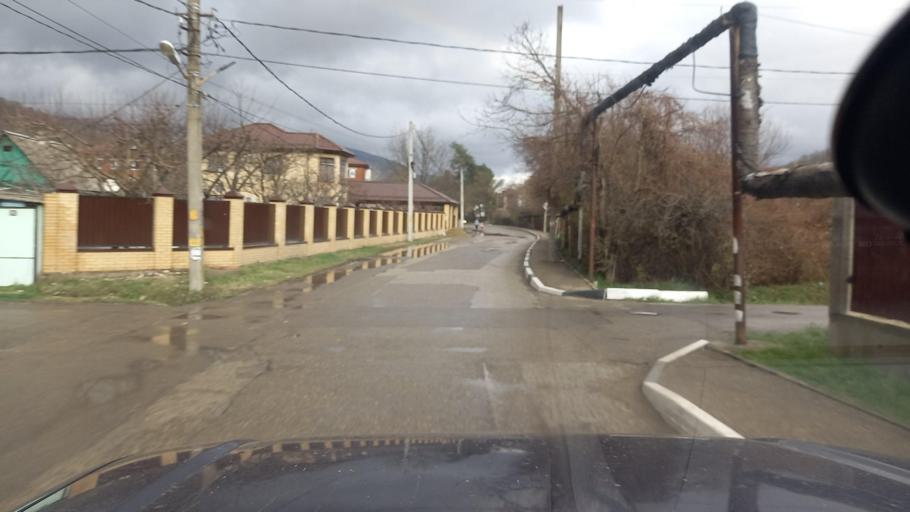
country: RU
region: Krasnodarskiy
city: Pshada
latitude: 44.4740
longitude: 38.3980
